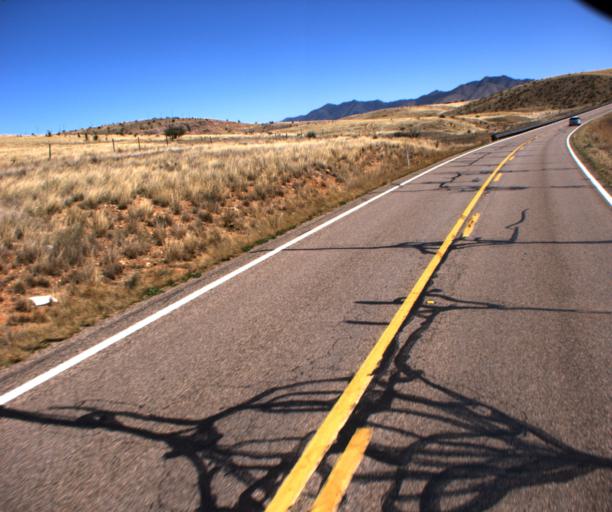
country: US
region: Arizona
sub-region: Cochise County
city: Huachuca City
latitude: 31.7149
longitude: -110.5573
